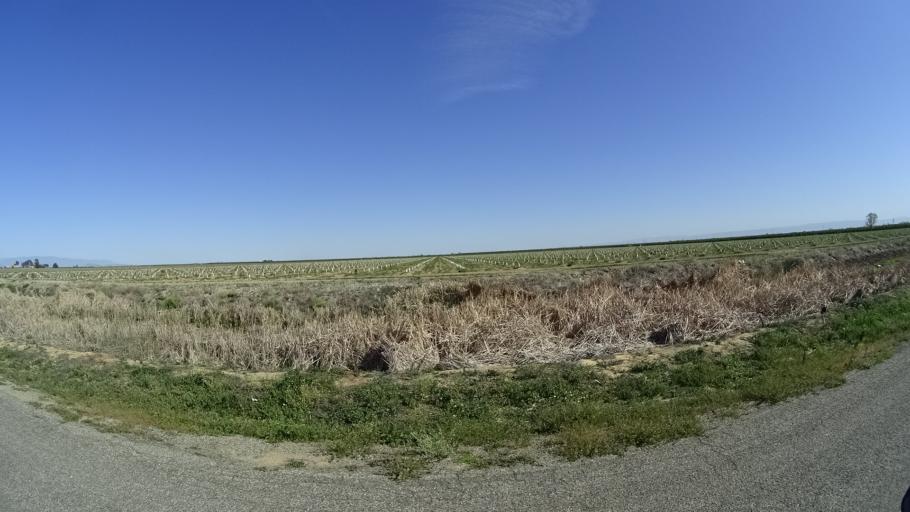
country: US
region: California
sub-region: Glenn County
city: Willows
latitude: 39.6112
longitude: -122.1426
